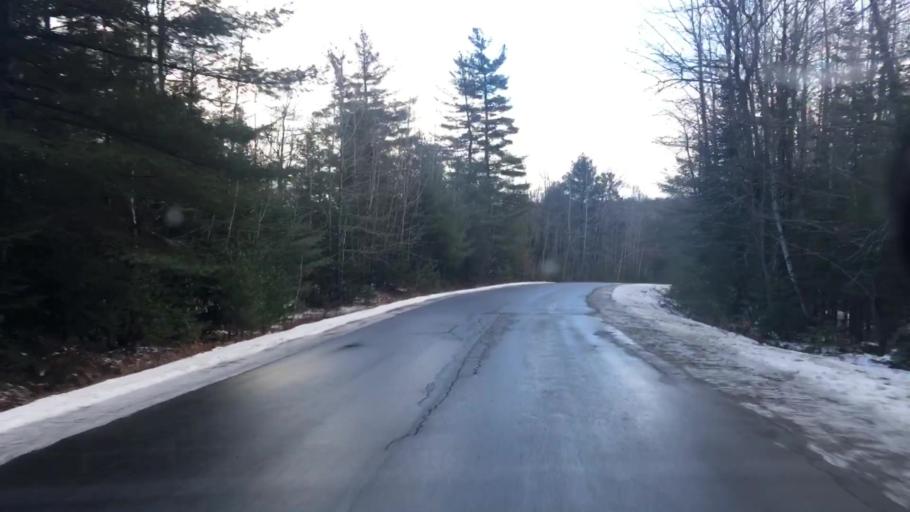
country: US
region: Maine
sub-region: Hancock County
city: Dedham
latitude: 44.6897
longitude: -68.7170
